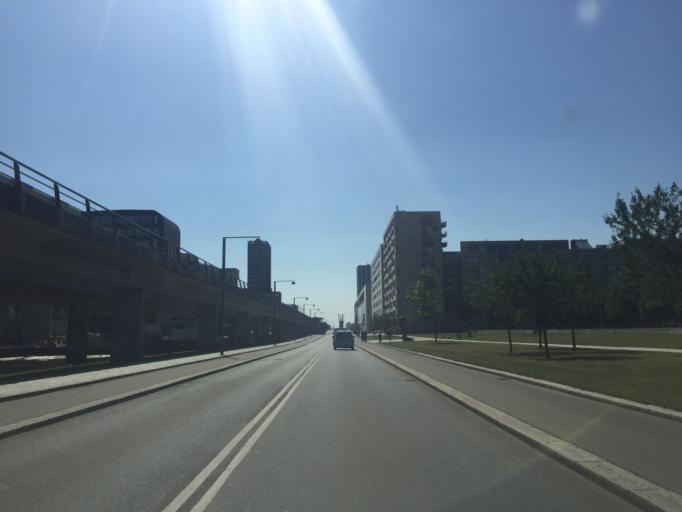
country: DK
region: Capital Region
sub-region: Tarnby Kommune
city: Tarnby
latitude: 55.6339
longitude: 12.5810
